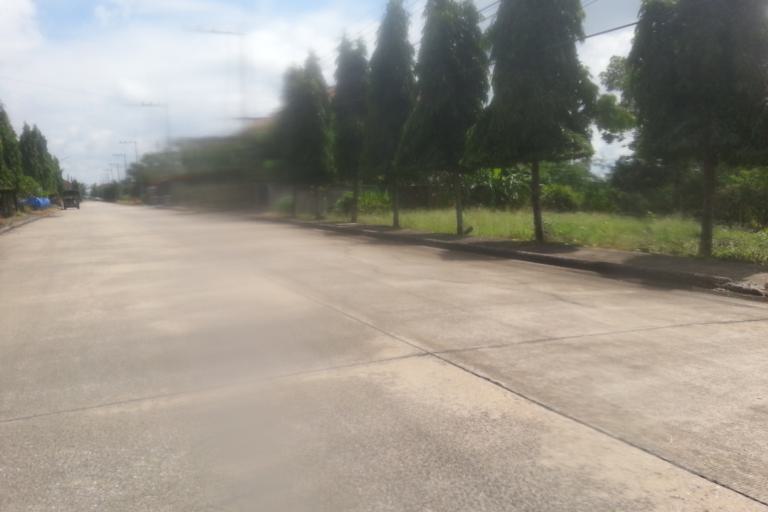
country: TH
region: Pathum Thani
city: Nong Suea
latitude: 14.0606
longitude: 100.8604
